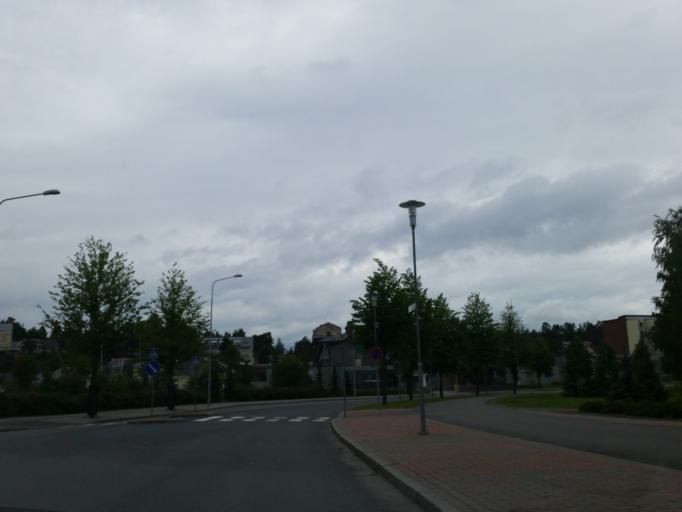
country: FI
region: Northern Savo
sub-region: Kuopio
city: Kuopio
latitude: 62.8947
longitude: 27.6926
